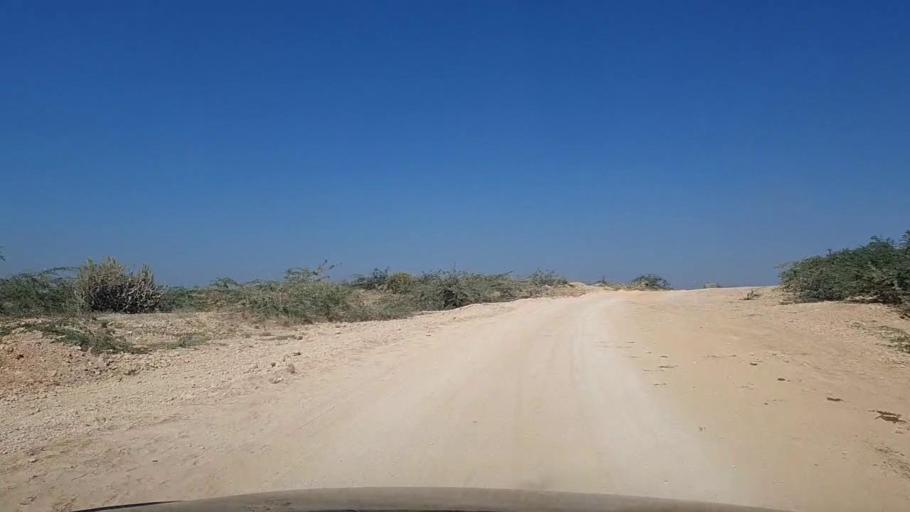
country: PK
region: Sindh
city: Thatta
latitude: 24.6204
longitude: 67.8397
